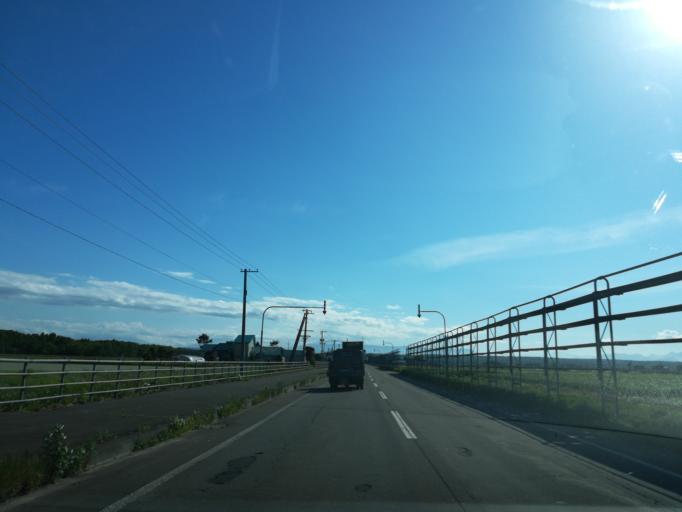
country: JP
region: Hokkaido
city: Kitahiroshima
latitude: 43.0434
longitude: 141.5897
